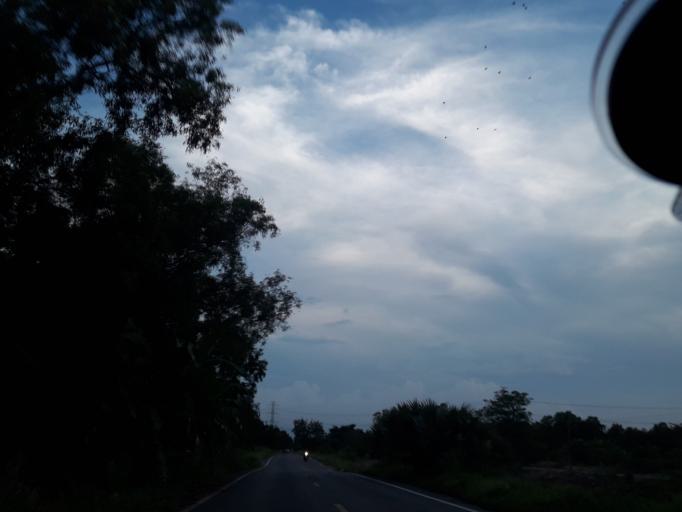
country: TH
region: Pathum Thani
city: Nong Suea
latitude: 14.1921
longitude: 100.8689
